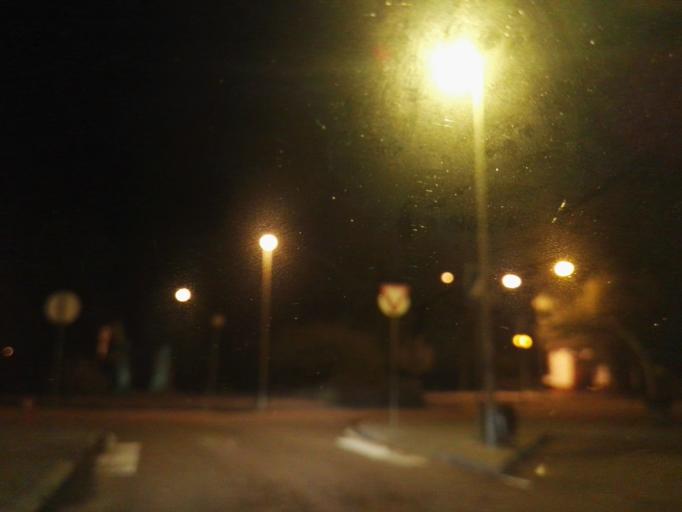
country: PT
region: Evora
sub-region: Estremoz
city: Estremoz
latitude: 38.8005
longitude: -7.6611
